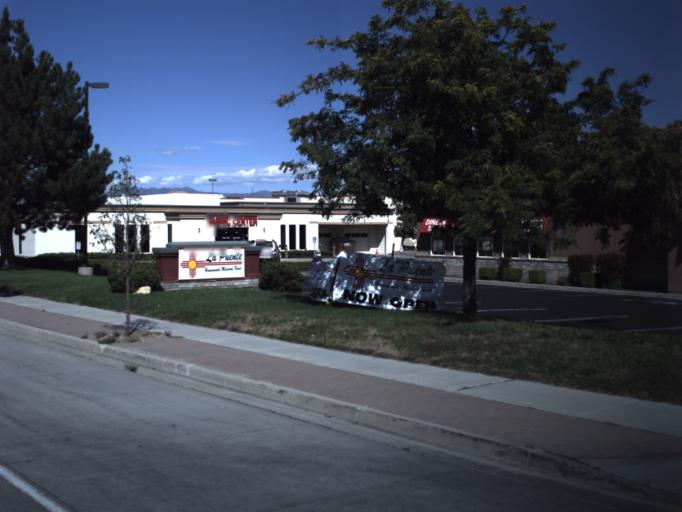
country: US
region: Utah
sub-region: Salt Lake County
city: South Jordan Heights
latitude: 40.5847
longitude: -111.9386
